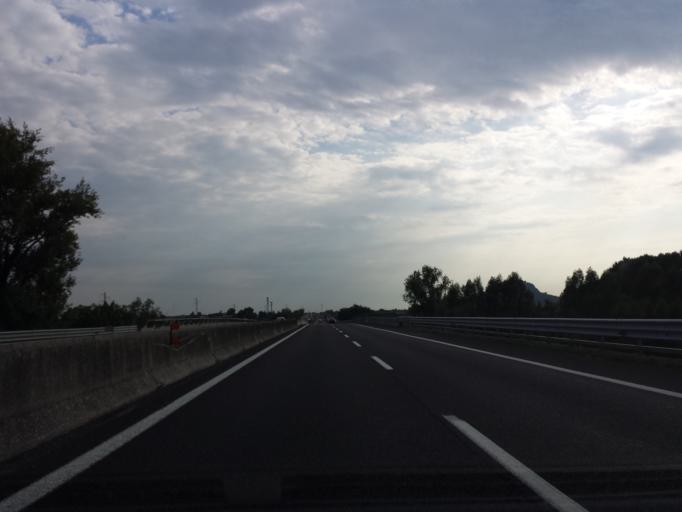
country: IT
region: Veneto
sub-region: Provincia di Padova
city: Pernumia
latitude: 45.2662
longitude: 11.7815
